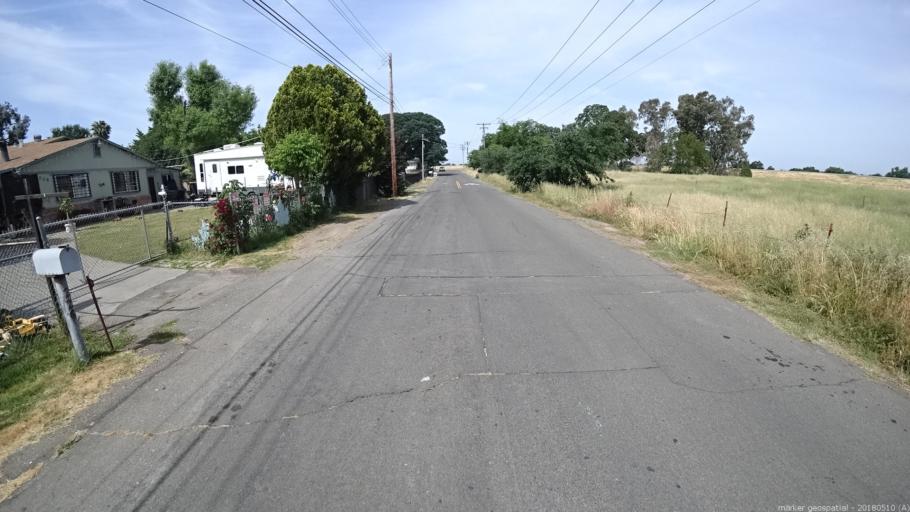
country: US
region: California
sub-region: Sacramento County
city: Rio Linda
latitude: 38.6603
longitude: -121.4597
